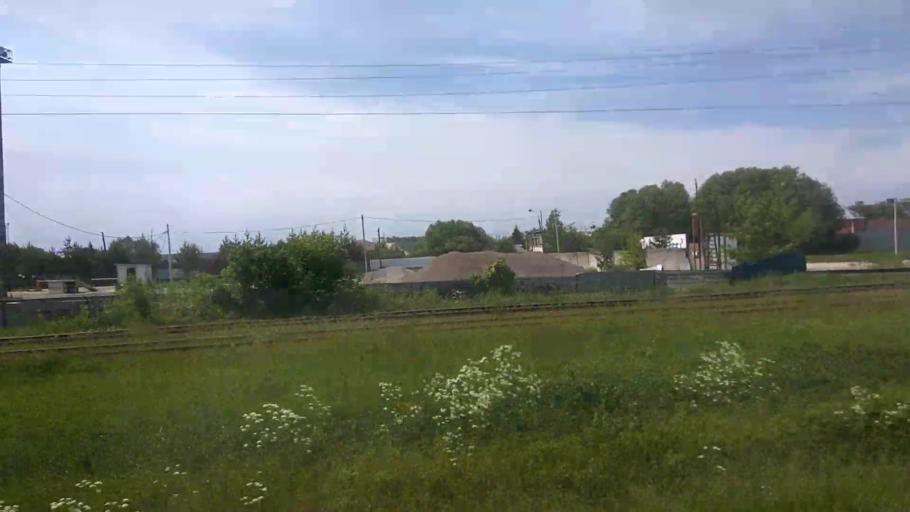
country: RU
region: Moskovskaya
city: Malyshevo
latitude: 55.5079
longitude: 38.3478
